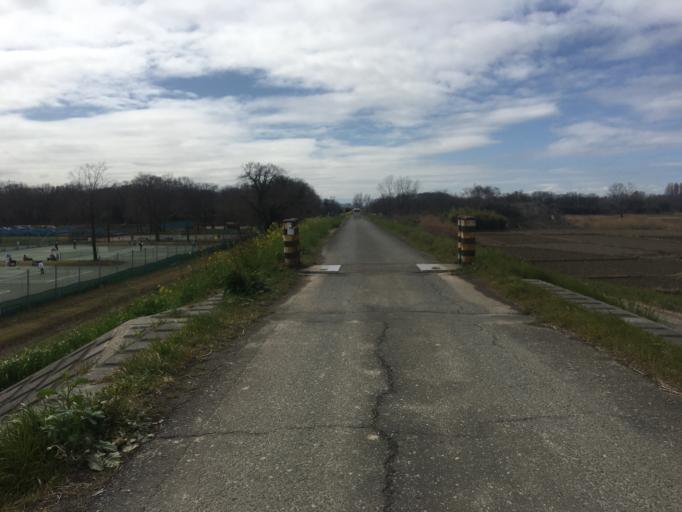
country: JP
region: Saitama
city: Shiki
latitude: 35.8527
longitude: 139.6089
